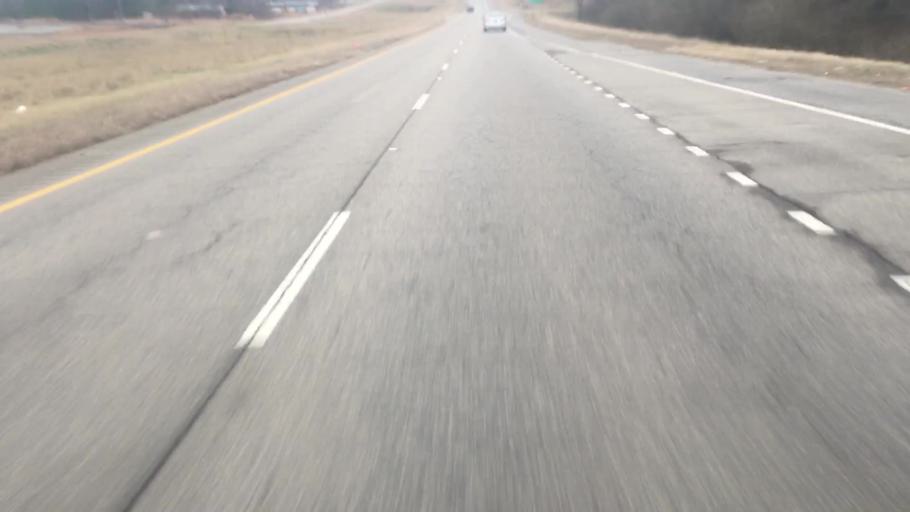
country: US
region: Alabama
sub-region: Walker County
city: Cordova
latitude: 33.8049
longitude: -87.1325
